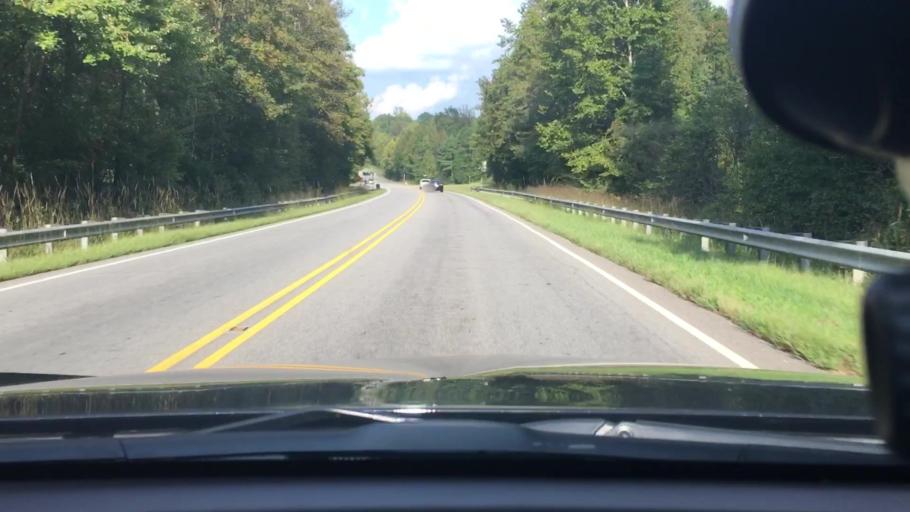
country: US
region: North Carolina
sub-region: Randolph County
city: Asheboro
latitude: 35.6672
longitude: -79.8832
